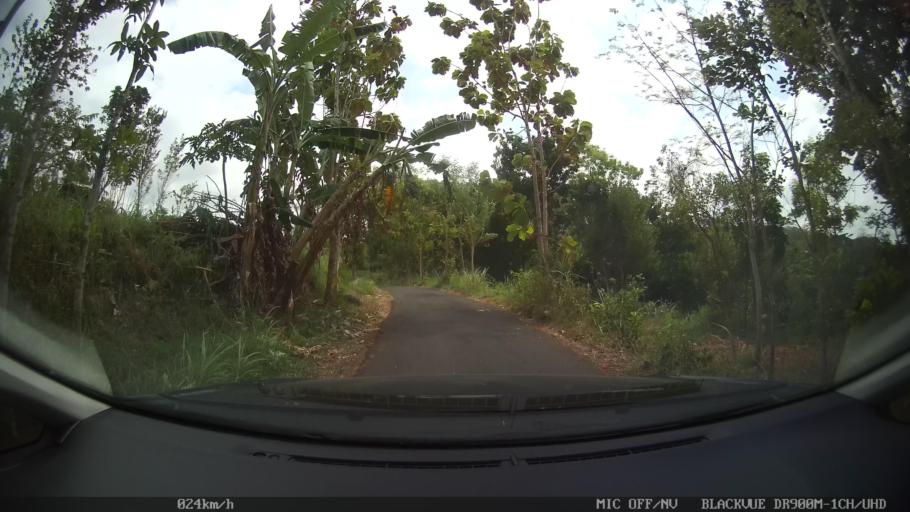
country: ID
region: Central Java
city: Candi Prambanan
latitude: -7.8165
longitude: 110.5253
